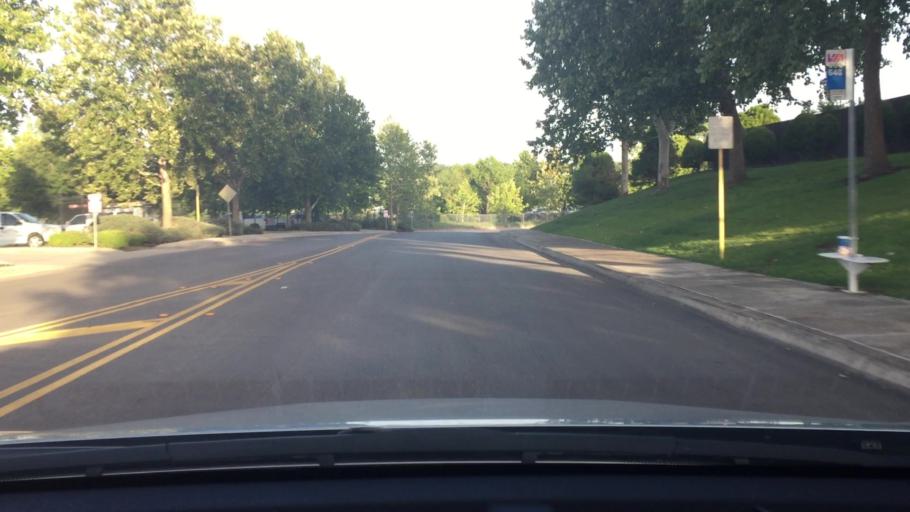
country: US
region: Texas
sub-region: Bexar County
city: Hollywood Park
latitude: 29.5535
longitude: -98.4648
